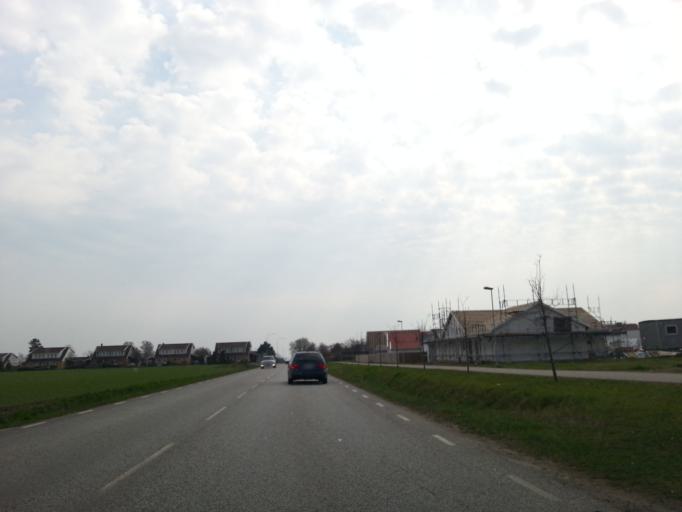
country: SE
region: Skane
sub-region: Trelleborgs Kommun
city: Trelleborg
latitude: 55.3589
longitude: 13.2380
